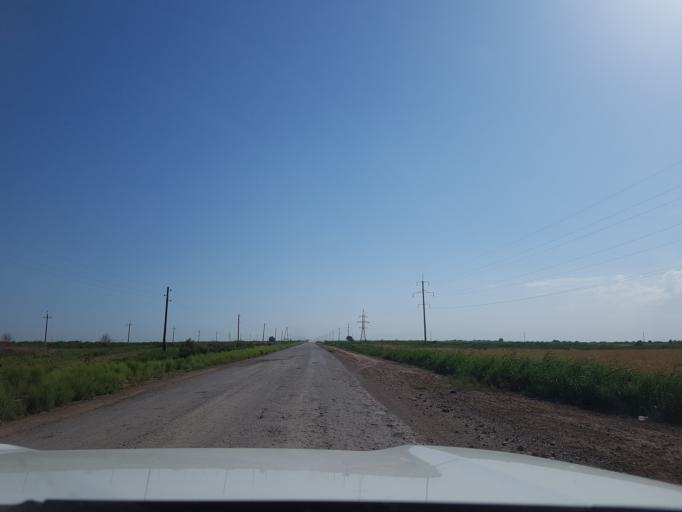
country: TM
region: Dasoguz
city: Koeneuergench
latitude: 42.1072
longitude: 58.9122
